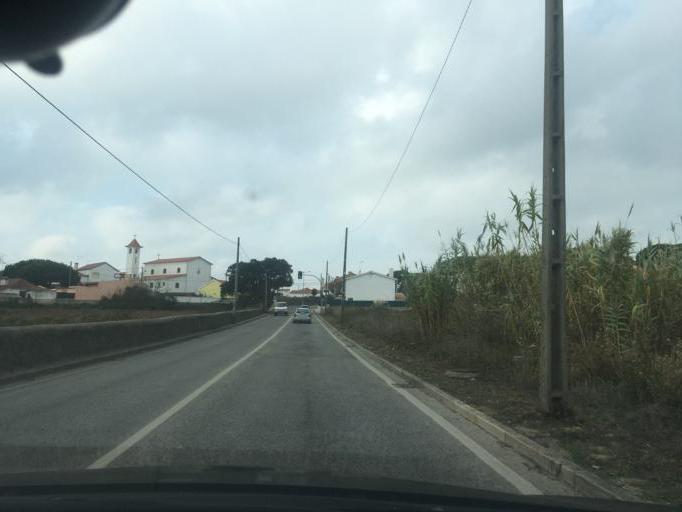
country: PT
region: Lisbon
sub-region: Sintra
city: Sintra
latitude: 38.8366
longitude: -9.3648
